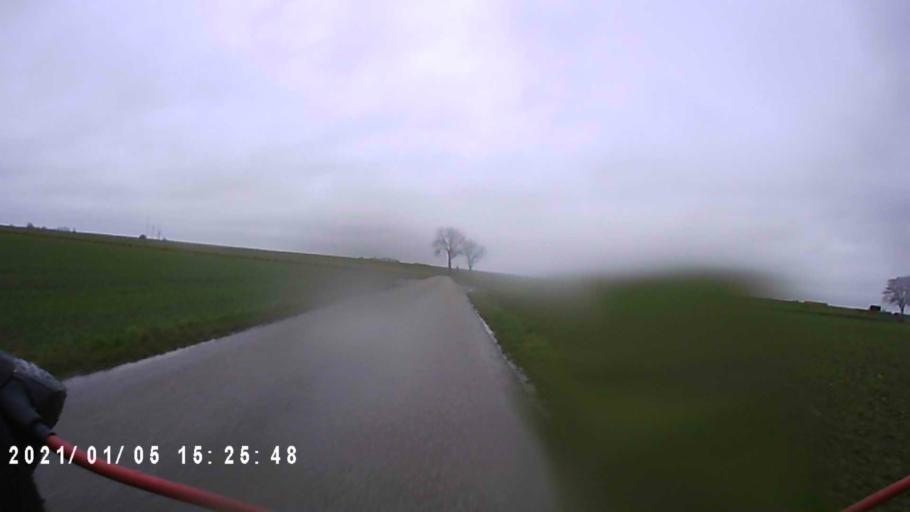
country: DE
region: Lower Saxony
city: Bunde
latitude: 53.2246
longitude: 7.1995
